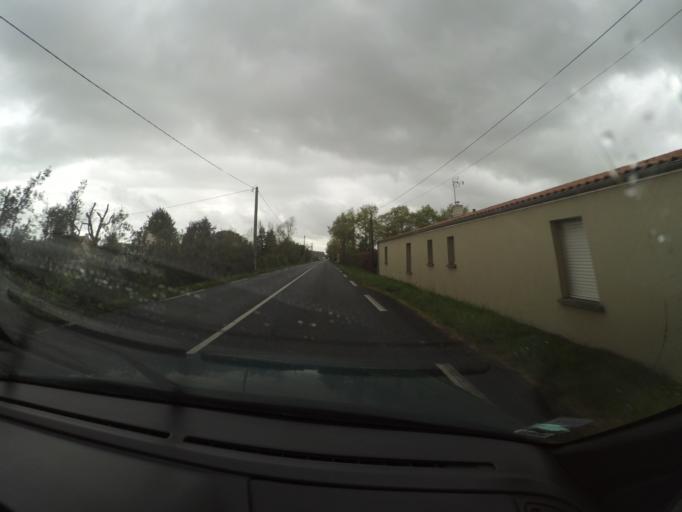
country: FR
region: Pays de la Loire
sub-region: Departement de la Loire-Atlantique
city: Vallet
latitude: 47.1842
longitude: -1.2563
